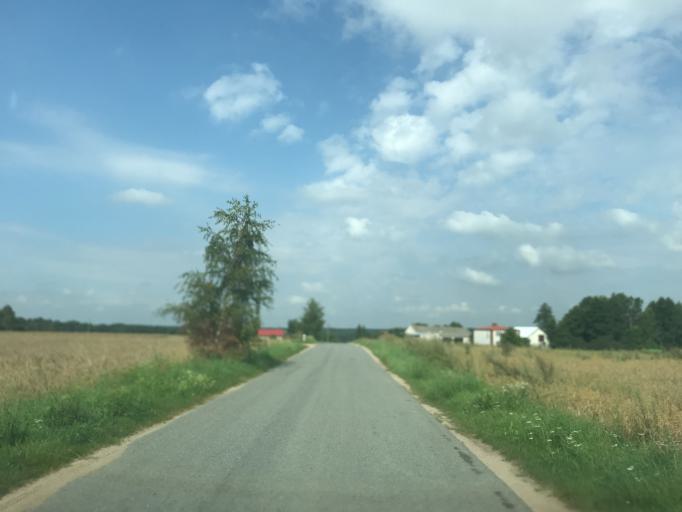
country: PL
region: Warmian-Masurian Voivodeship
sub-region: Powiat nowomiejski
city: Kurzetnik
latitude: 53.4002
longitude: 19.4621
